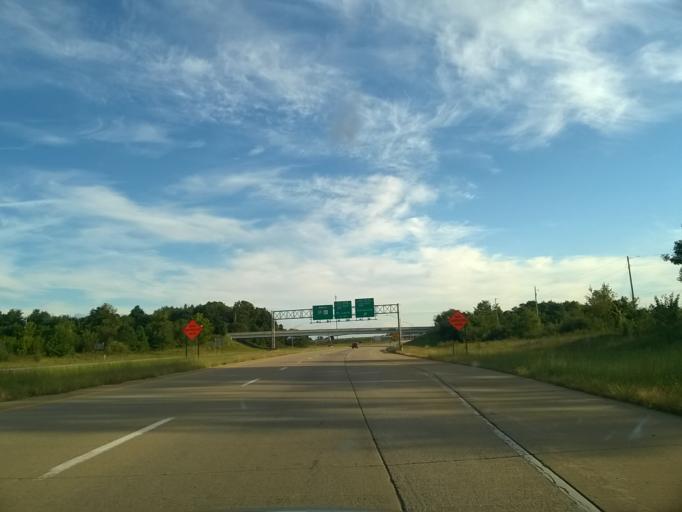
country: US
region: Indiana
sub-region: Gibson County
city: Haubstadt
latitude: 38.1642
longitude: -87.4720
